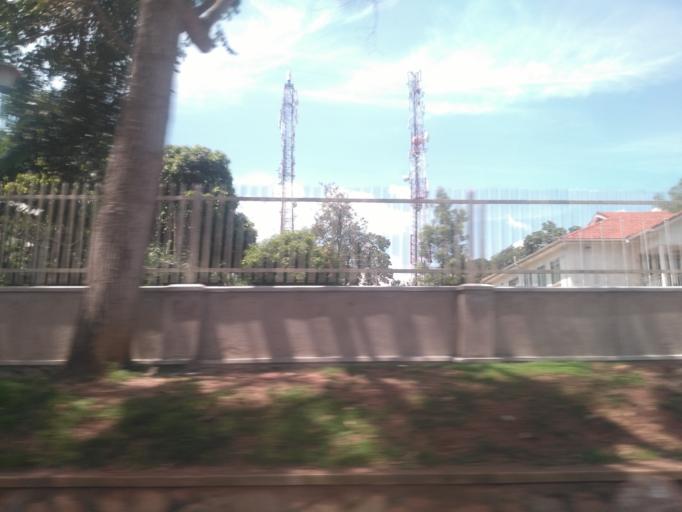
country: UG
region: Central Region
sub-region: Wakiso District
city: Entebbe
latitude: 0.0524
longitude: 32.4667
